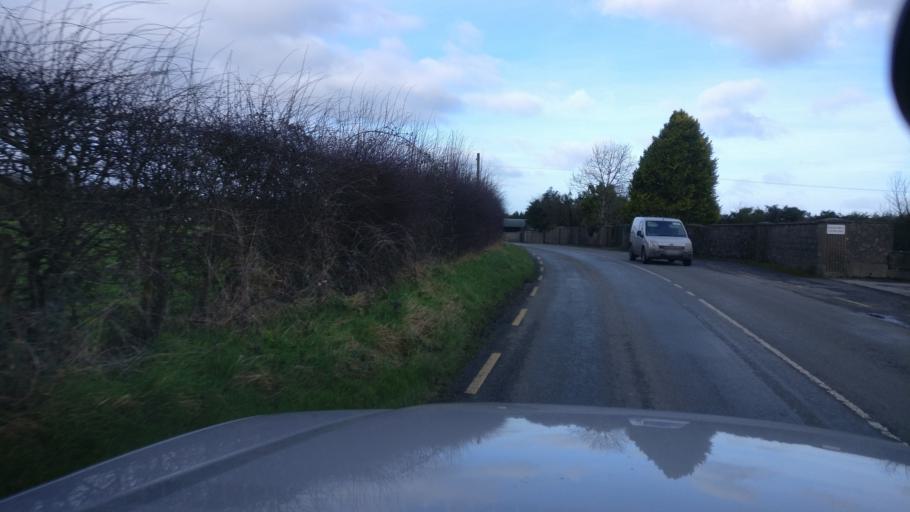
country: IE
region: Leinster
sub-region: Kilkenny
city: Castlecomer
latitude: 52.8118
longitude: -7.2117
